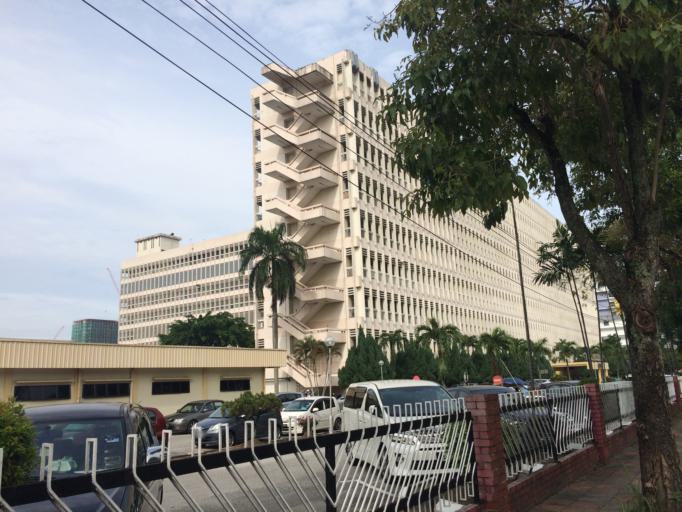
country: MY
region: Perak
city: Ipoh
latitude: 4.6044
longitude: 101.0918
